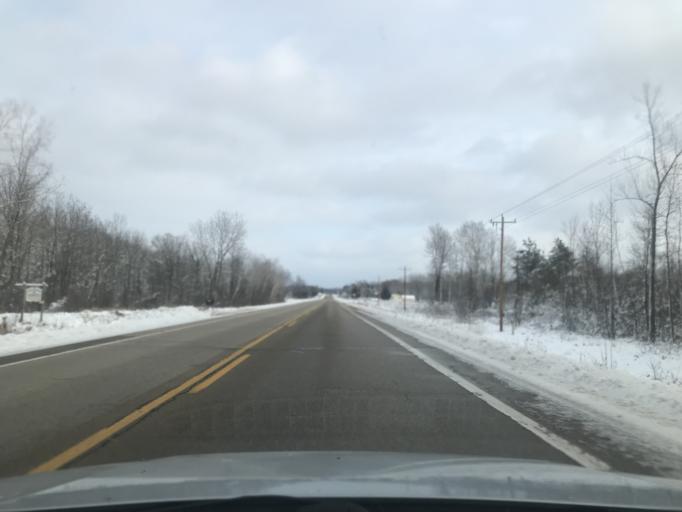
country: US
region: Wisconsin
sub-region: Oconto County
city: Oconto Falls
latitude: 44.8868
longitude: -88.0335
